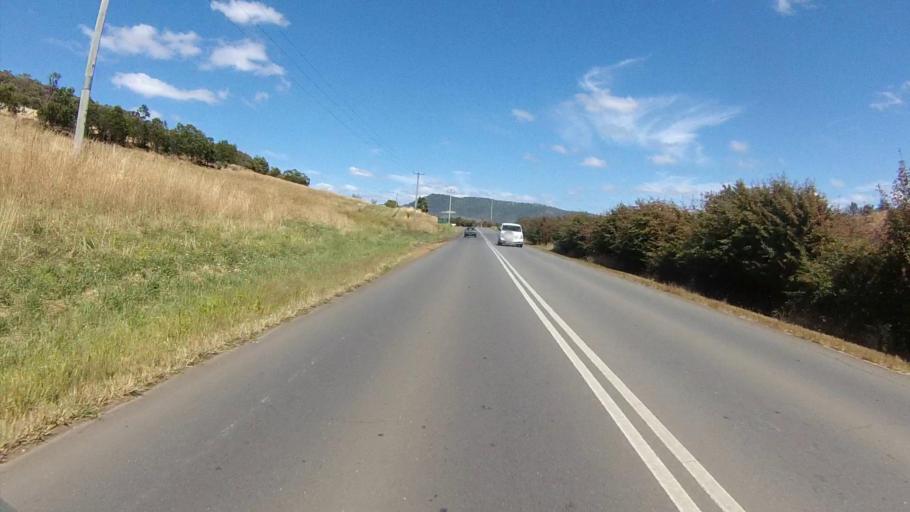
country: AU
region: Tasmania
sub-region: Clarence
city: Cambridge
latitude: -42.7400
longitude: 147.4248
